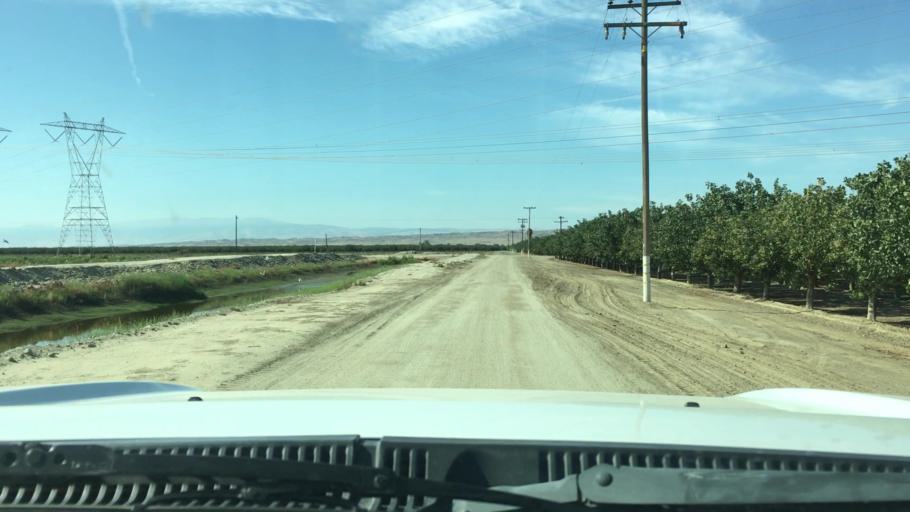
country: US
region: California
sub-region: Kern County
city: Buttonwillow
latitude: 35.3713
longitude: -119.3857
